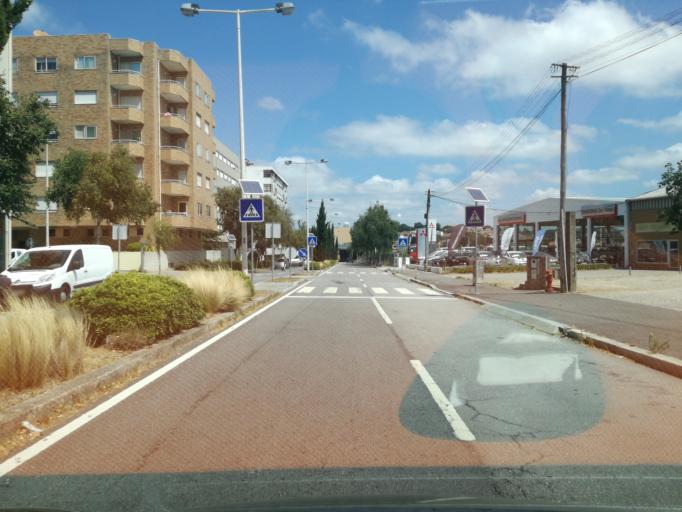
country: PT
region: Porto
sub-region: Maia
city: Maia
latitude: 41.2378
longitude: -8.6090
